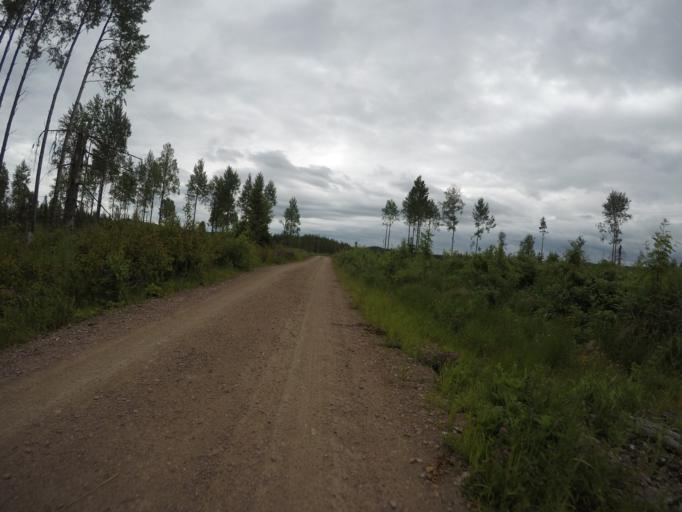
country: SE
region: Dalarna
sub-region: Ludvika Kommun
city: Abborrberget
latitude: 60.0794
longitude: 14.5573
